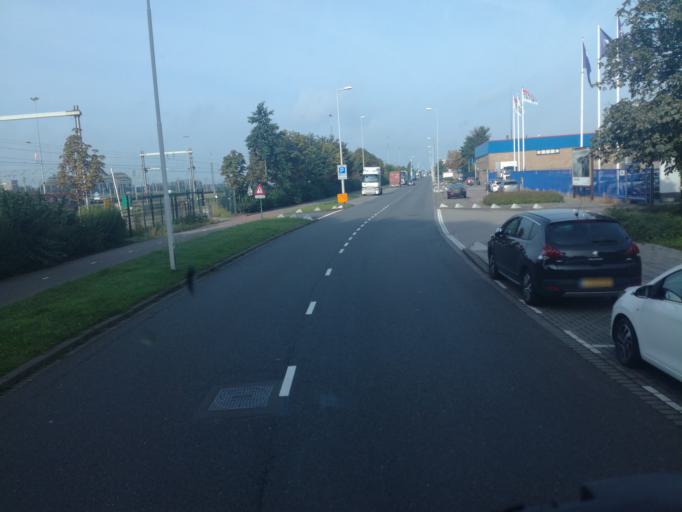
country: NL
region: South Holland
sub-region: Gemeente Rotterdam
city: Delfshaven
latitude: 51.8723
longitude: 4.4516
